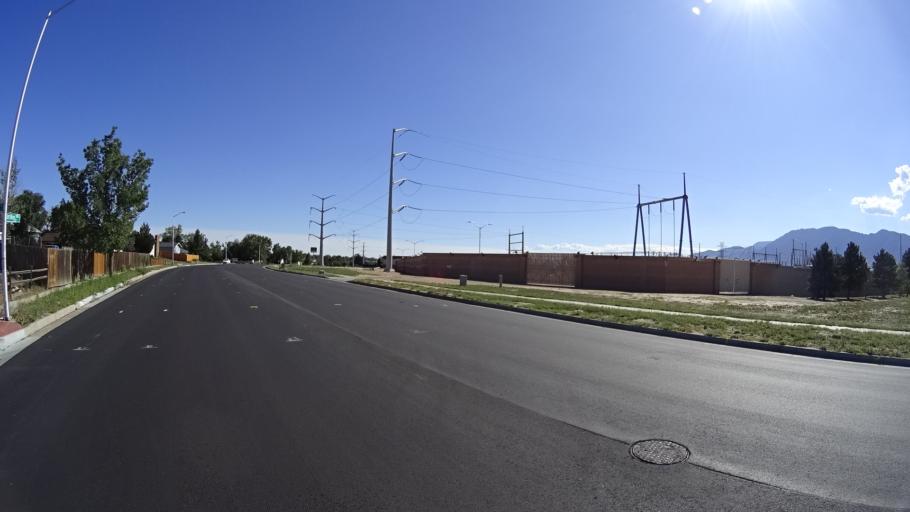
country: US
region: Colorado
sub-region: El Paso County
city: Stratmoor
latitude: 38.7935
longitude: -104.7546
